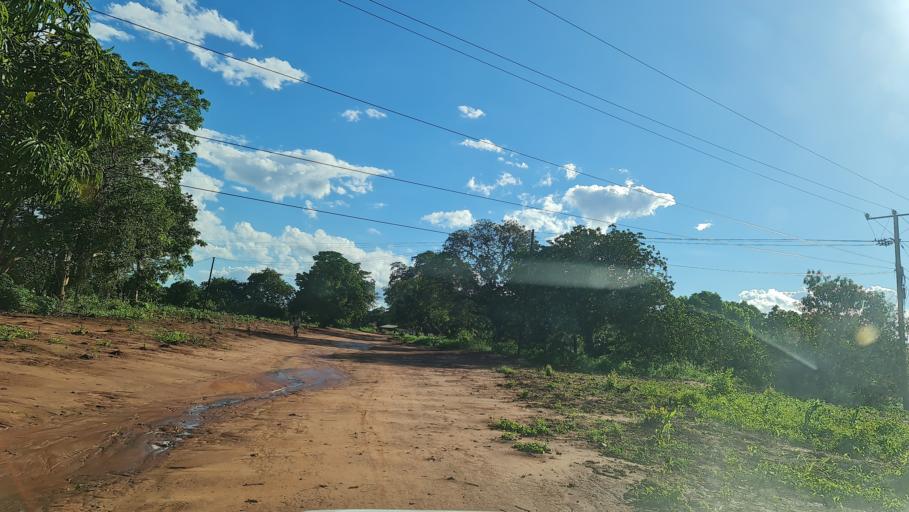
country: MZ
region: Nampula
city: Ilha de Mocambique
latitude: -14.9148
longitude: 40.2170
